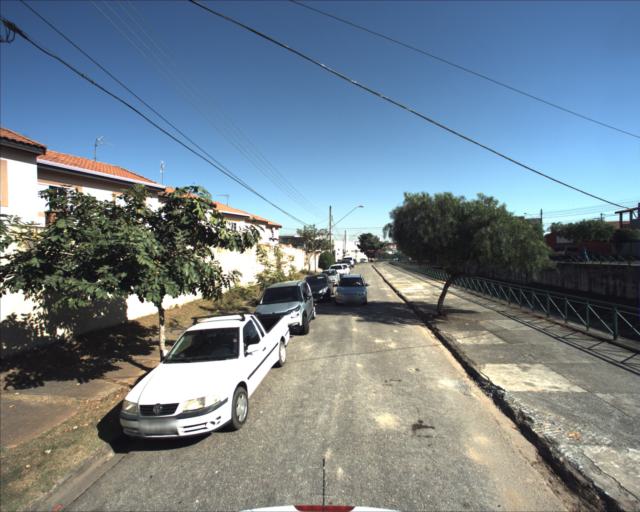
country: BR
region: Sao Paulo
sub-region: Sorocaba
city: Sorocaba
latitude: -23.5125
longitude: -47.4283
